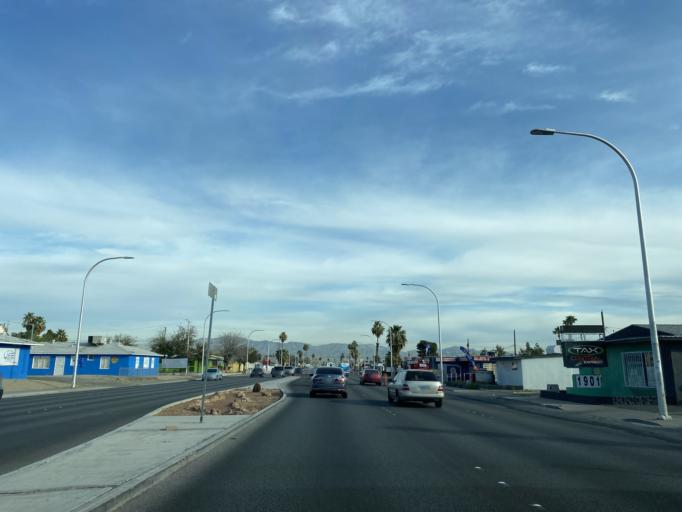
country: US
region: Nevada
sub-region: Clark County
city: Winchester
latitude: 36.1488
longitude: -115.1188
